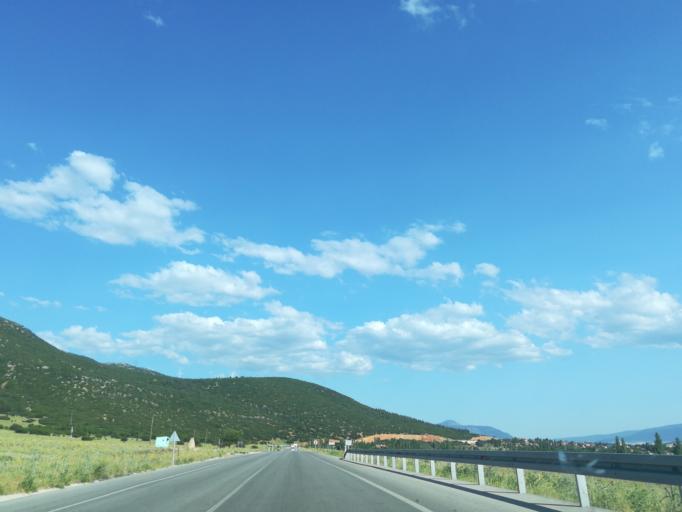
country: TR
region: Denizli
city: Ishakli
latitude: 38.1651
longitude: 30.0741
